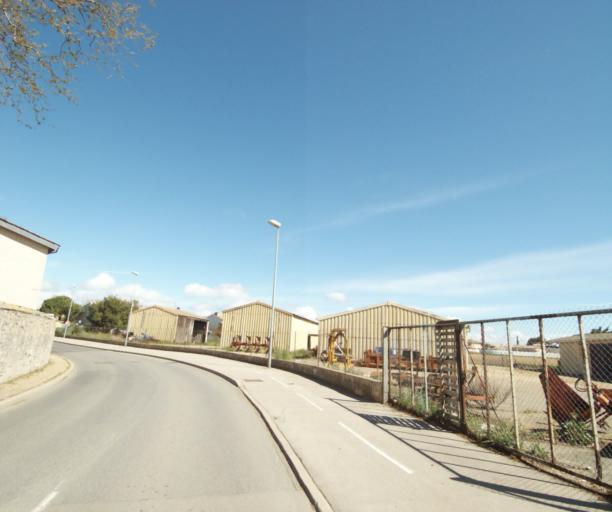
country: FR
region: Languedoc-Roussillon
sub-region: Departement de l'Herault
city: Villeneuve-les-Maguelone
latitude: 43.5322
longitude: 3.8651
